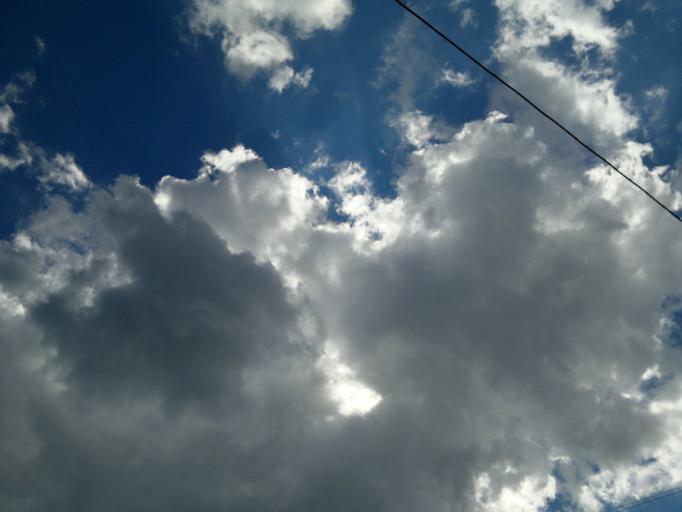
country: RU
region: St.-Petersburg
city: Saint Petersburg
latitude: 59.9267
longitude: 30.2966
